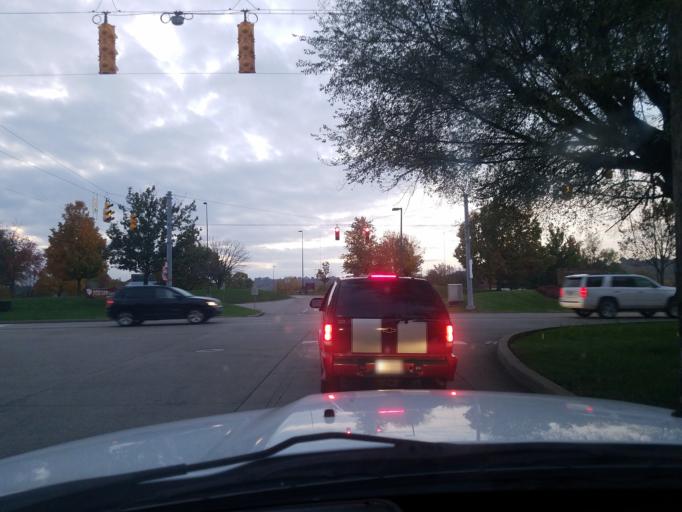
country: US
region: Indiana
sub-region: Floyd County
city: New Albany
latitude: 38.3457
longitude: -85.8162
